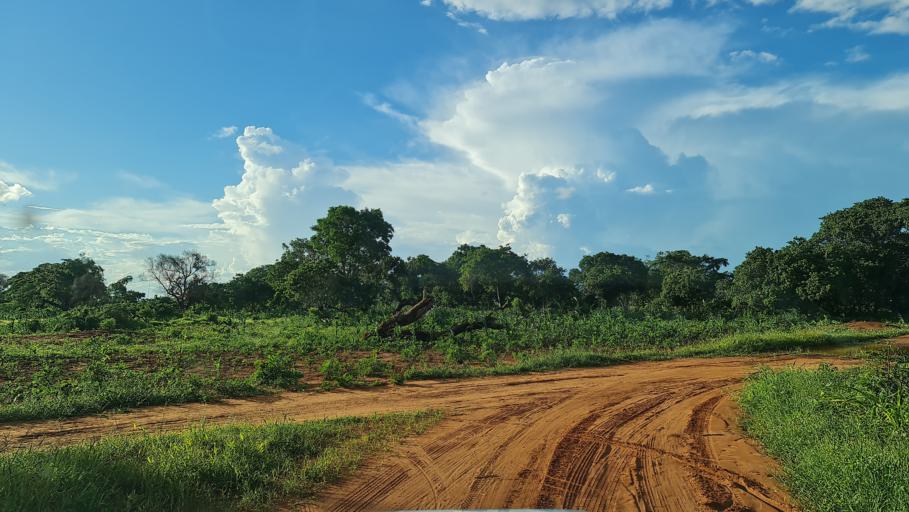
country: MZ
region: Nampula
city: Ilha de Mocambique
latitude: -14.9436
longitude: 40.1571
